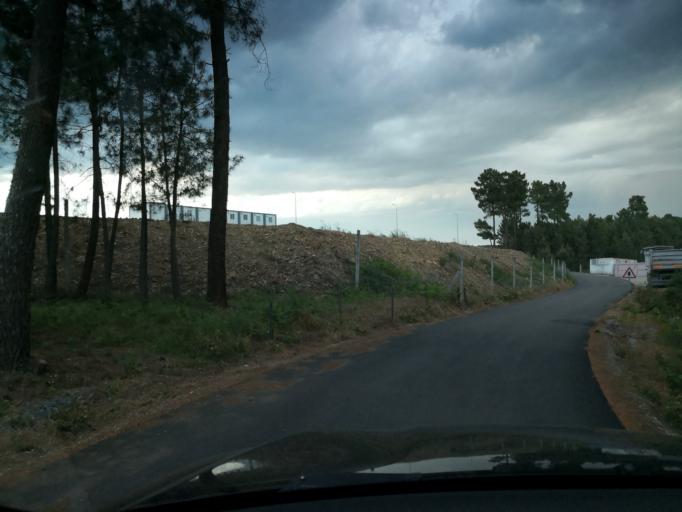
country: PT
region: Vila Real
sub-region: Vila Real
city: Vila Real
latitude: 41.2727
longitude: -7.6916
